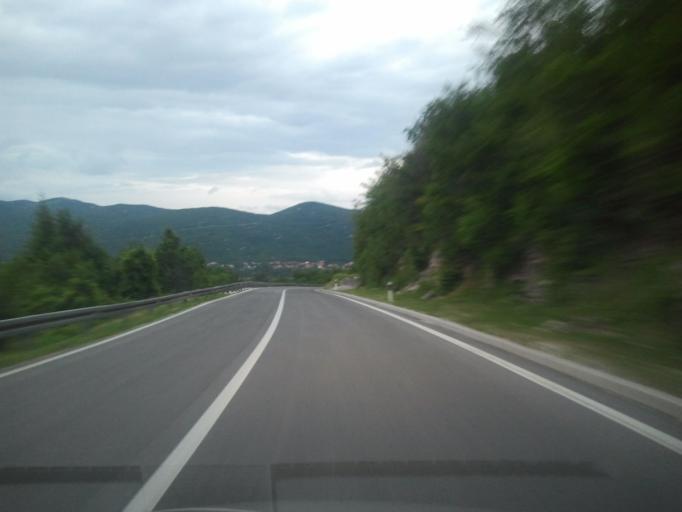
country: HR
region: Zadarska
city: Gracac
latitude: 44.2787
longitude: 15.8206
